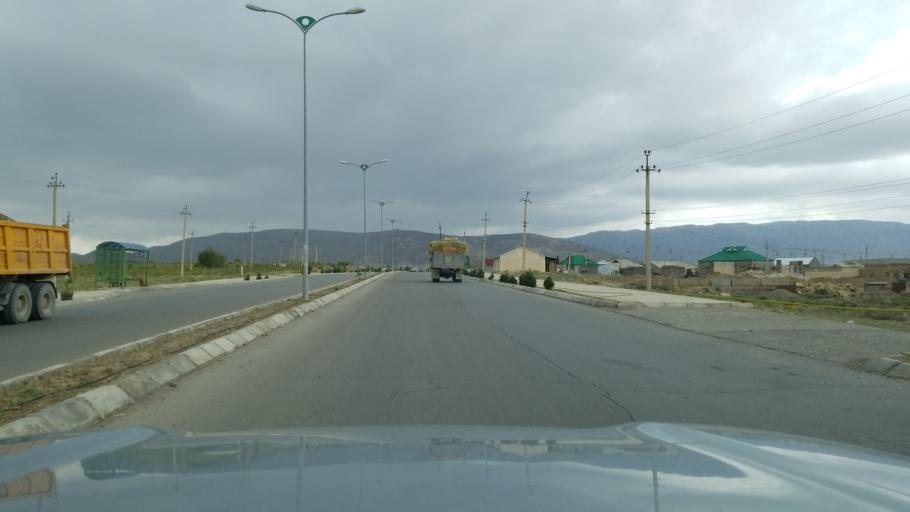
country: TM
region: Balkan
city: Serdar
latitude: 38.9667
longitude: 56.2944
